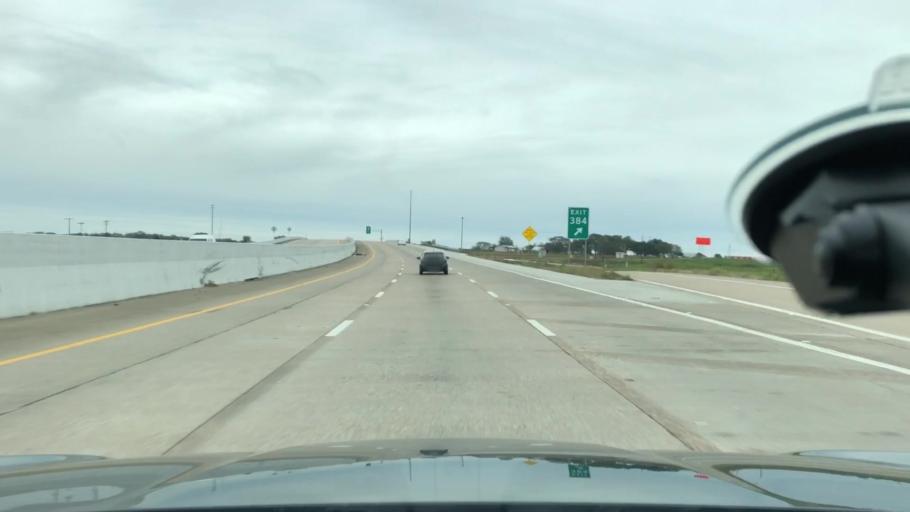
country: US
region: Texas
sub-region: Ellis County
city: Italy
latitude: 32.1738
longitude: -96.9108
